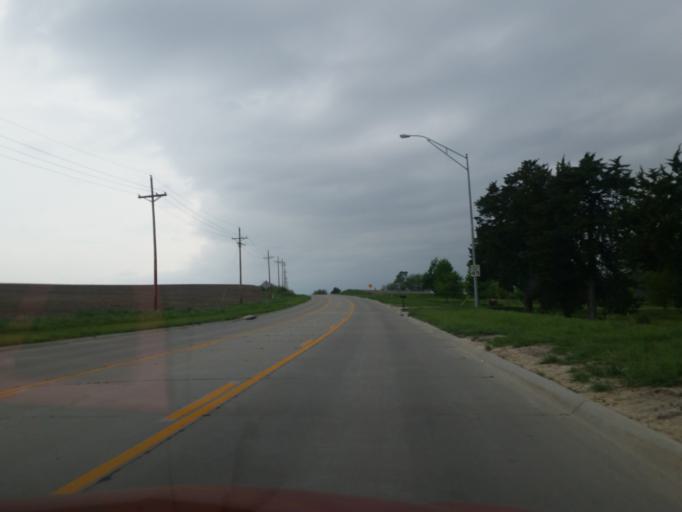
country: US
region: Nebraska
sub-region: Douglas County
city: Bennington
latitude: 41.3210
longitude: -96.1204
